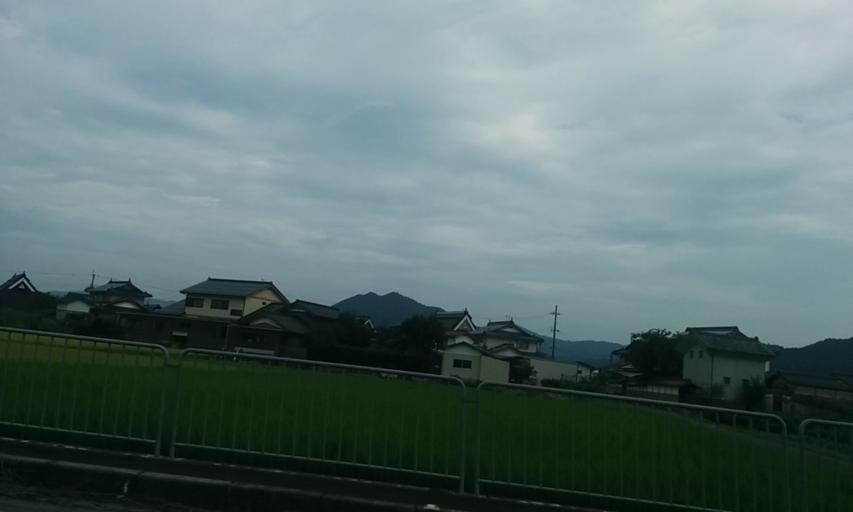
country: JP
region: Kyoto
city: Ayabe
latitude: 35.3142
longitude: 135.2237
